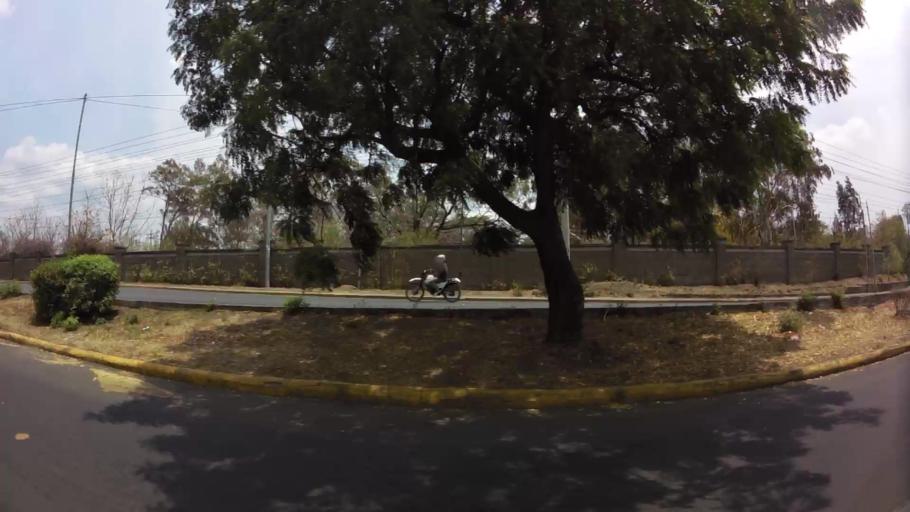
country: NI
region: Managua
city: Managua
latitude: 12.1159
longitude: -86.2854
